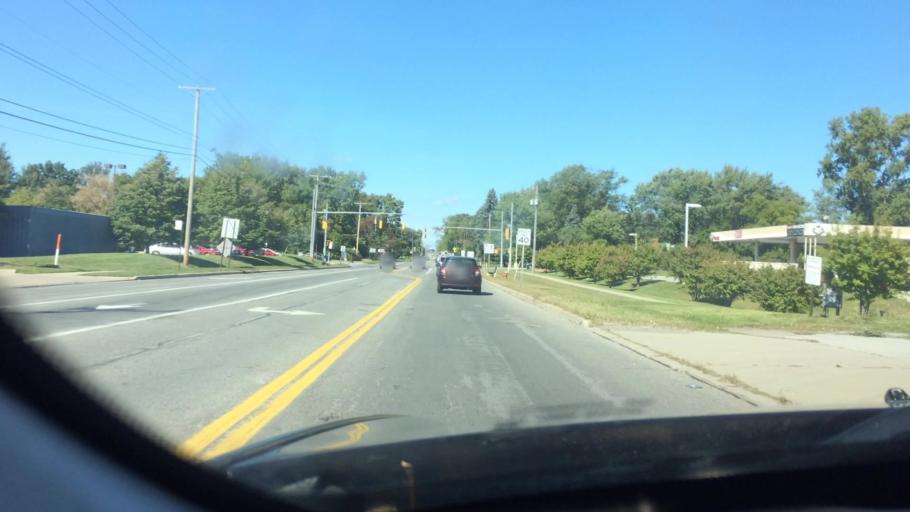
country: US
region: Ohio
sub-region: Lucas County
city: Ottawa Hills
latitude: 41.6620
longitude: -83.6825
